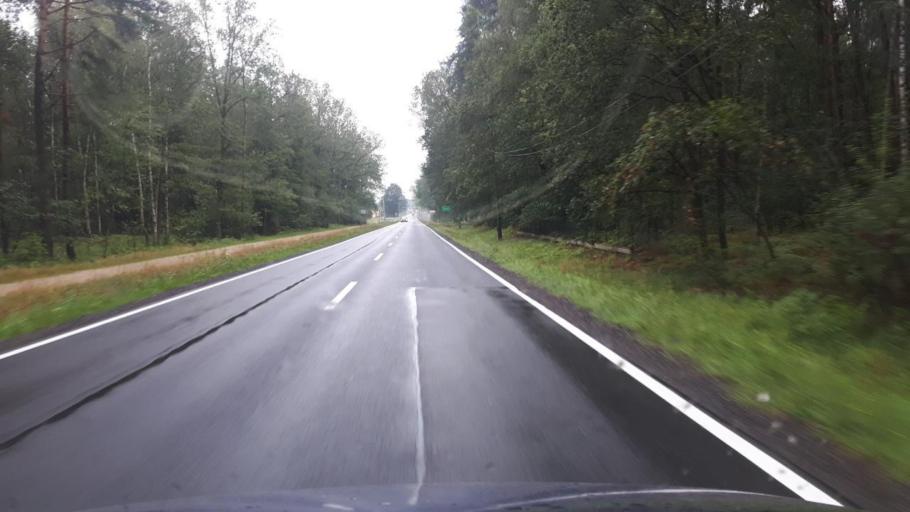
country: PL
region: Silesian Voivodeship
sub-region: Powiat lubliniecki
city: Ciasna
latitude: 50.7596
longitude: 18.6068
